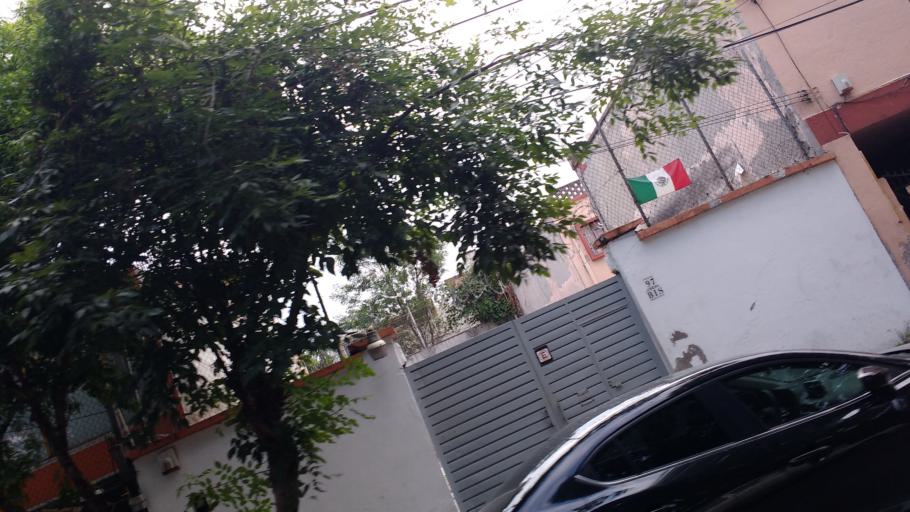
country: MX
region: Mexico City
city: Coyoacan
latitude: 19.3602
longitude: -99.1598
